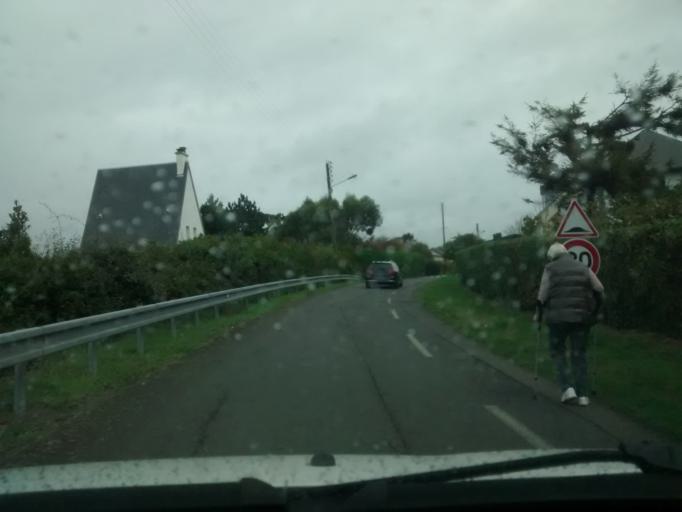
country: FR
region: Lower Normandy
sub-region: Departement de la Manche
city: Saint-Pair-sur-Mer
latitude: 48.8109
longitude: -1.5688
